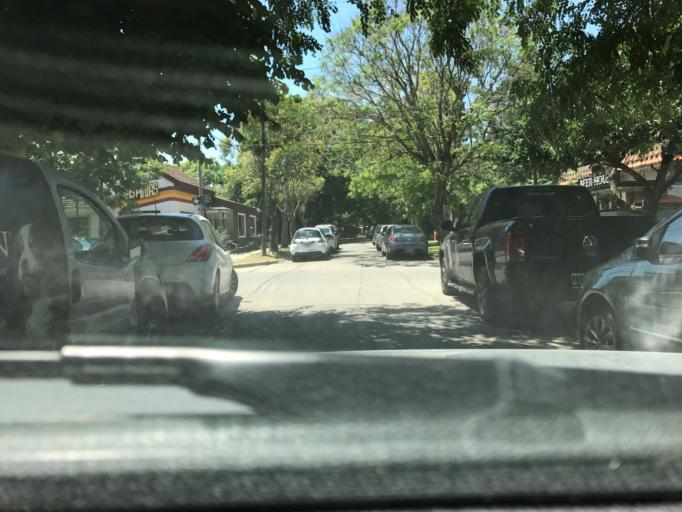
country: AR
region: Buenos Aires
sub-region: Partido de La Plata
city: La Plata
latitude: -34.8693
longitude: -58.0434
